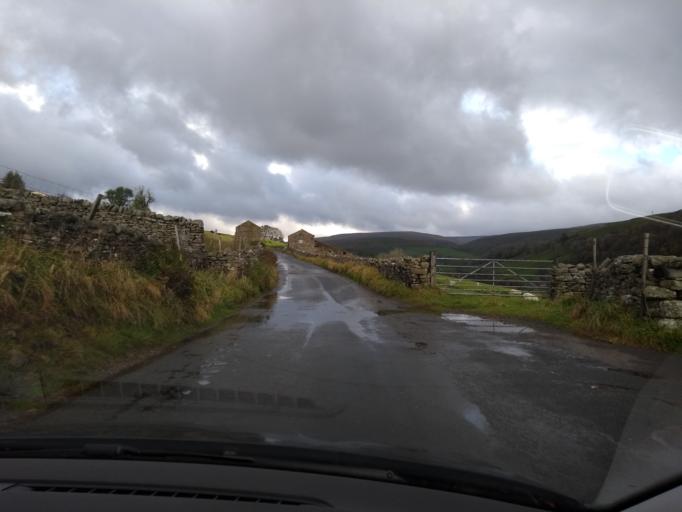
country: GB
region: England
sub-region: Cumbria
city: Kirkby Stephen
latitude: 54.3903
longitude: -2.1727
